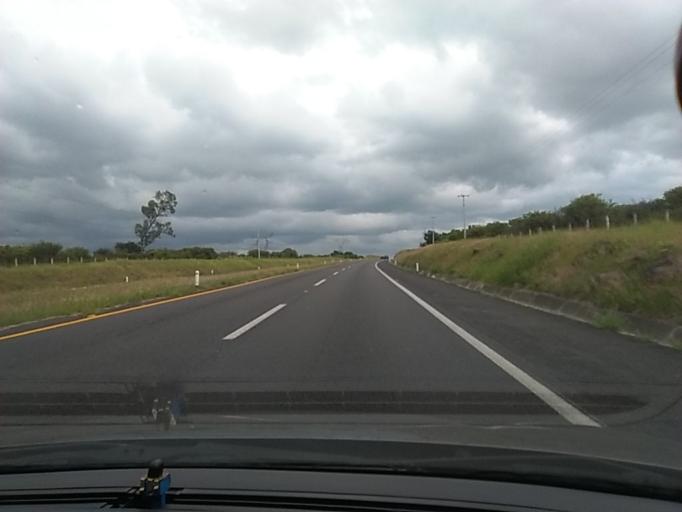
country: MX
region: Jalisco
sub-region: Zapotlanejo
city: La Mezquitera
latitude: 20.6005
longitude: -103.1185
